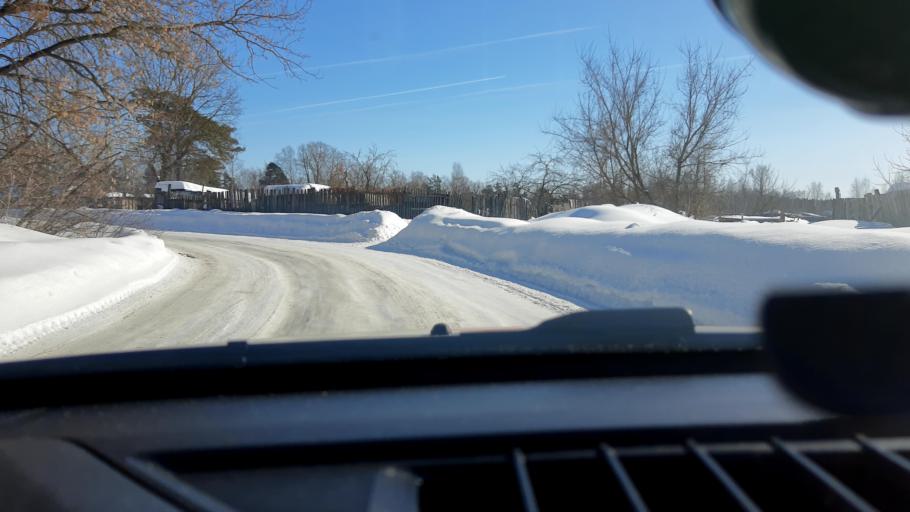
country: RU
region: Nizjnij Novgorod
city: Yuganets
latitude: 56.2448
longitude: 43.2291
